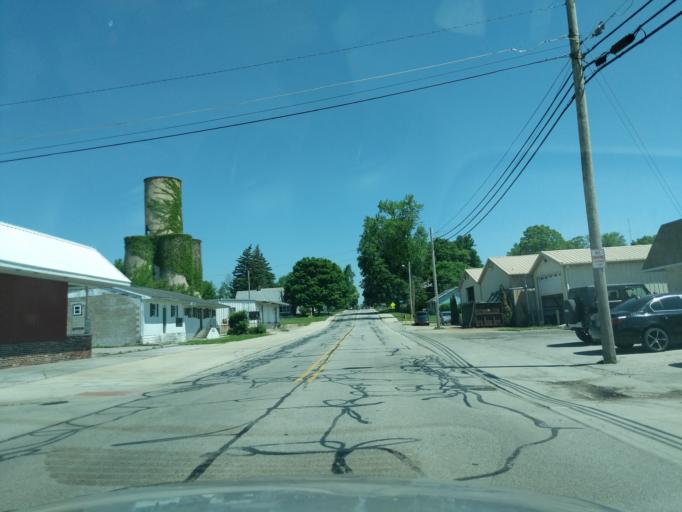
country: US
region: Indiana
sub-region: Whitley County
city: Columbia City
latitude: 41.1519
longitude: -85.4912
